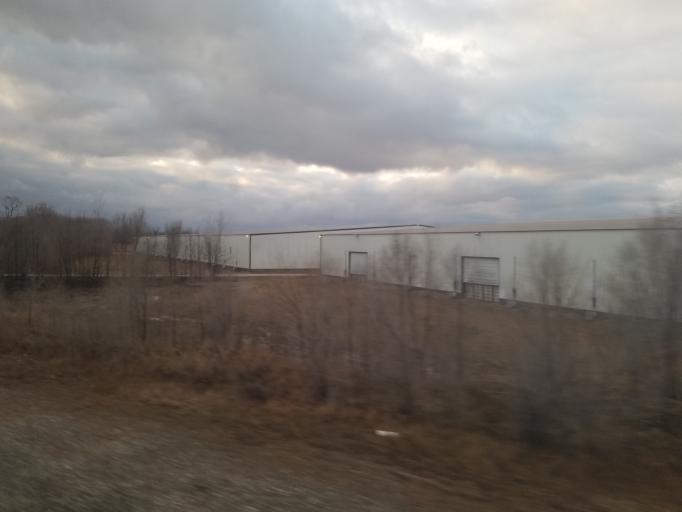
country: US
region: Illinois
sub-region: Henderson County
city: Oquawka
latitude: 40.8630
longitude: -90.9643
